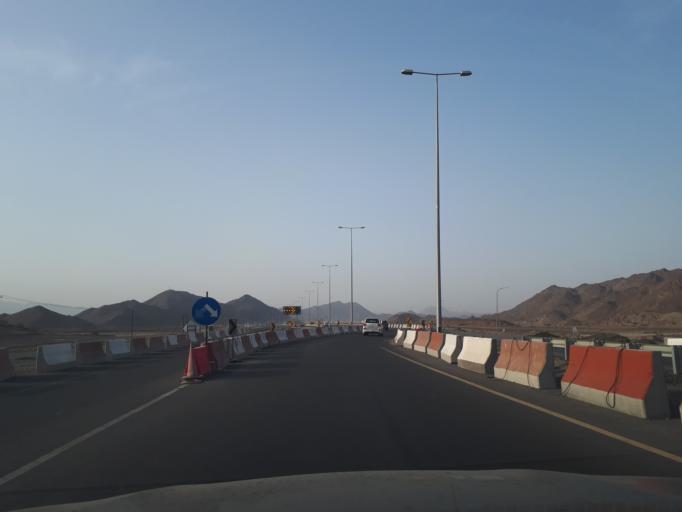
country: OM
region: Muhafazat ad Dakhiliyah
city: Sufalat Sama'il
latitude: 23.2925
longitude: 58.1098
